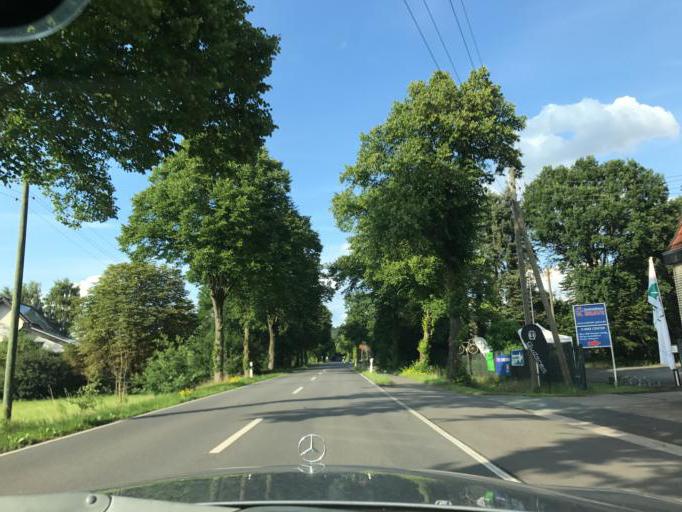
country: DE
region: Lower Saxony
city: Hasbergen
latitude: 52.2200
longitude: 7.9394
